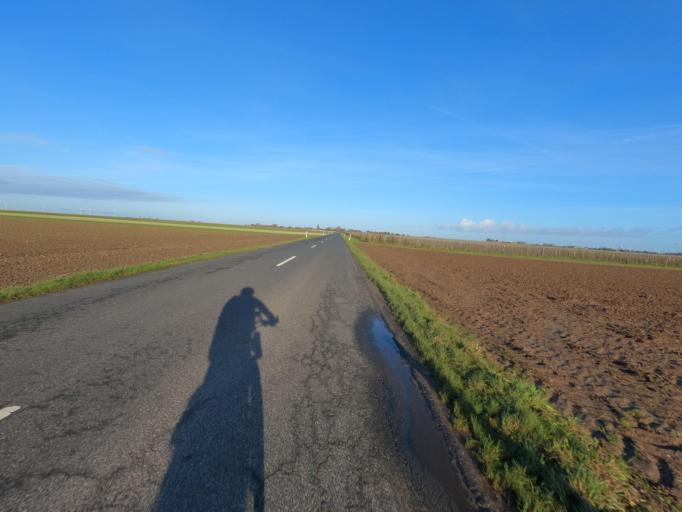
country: DE
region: North Rhine-Westphalia
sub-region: Regierungsbezirk Koln
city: Titz
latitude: 50.9666
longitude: 6.4115
